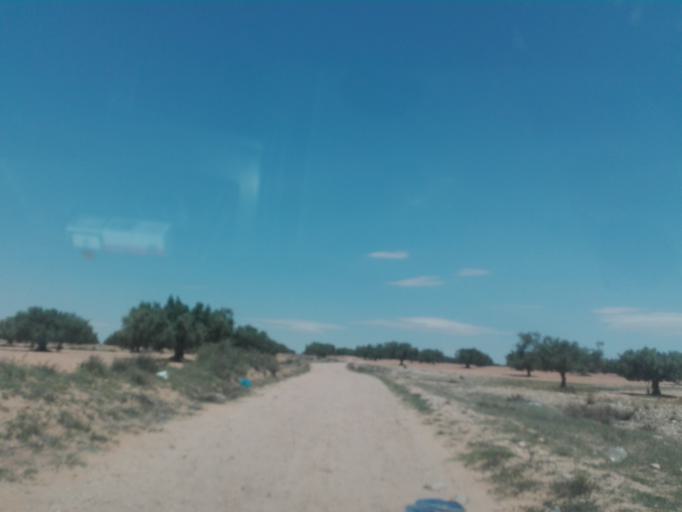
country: TN
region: Safaqis
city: Sfax
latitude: 34.6665
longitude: 10.6061
